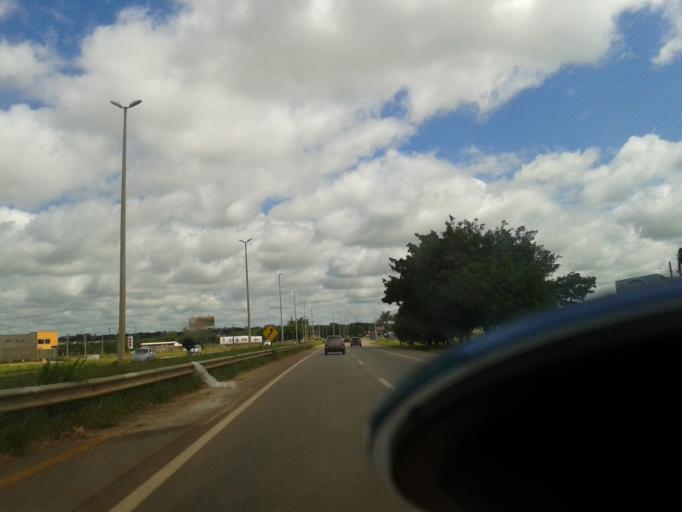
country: BR
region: Goias
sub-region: Goianira
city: Goianira
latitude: -16.5501
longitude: -49.4059
